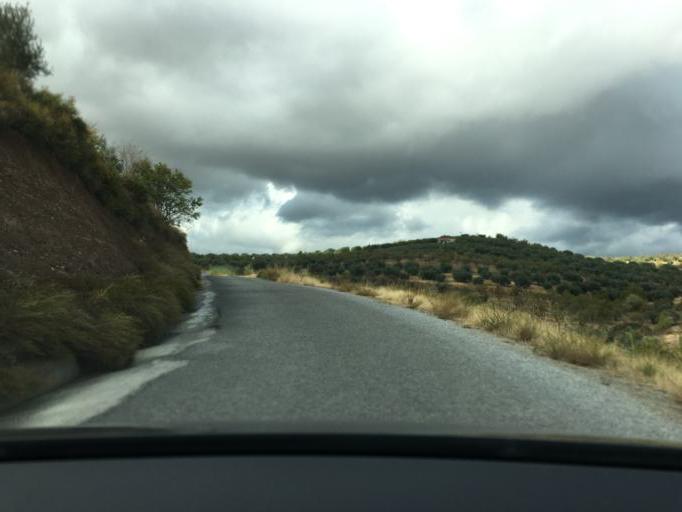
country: ES
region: Andalusia
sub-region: Provincia de Granada
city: Quentar
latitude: 37.2004
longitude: -3.4700
